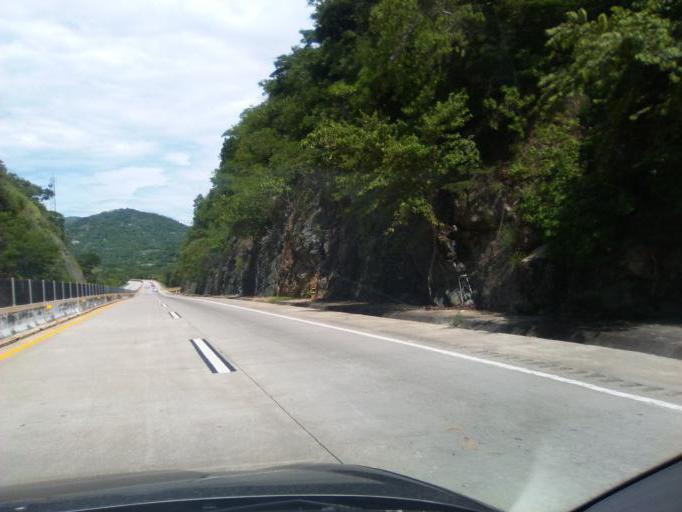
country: MX
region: Guerrero
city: Tierra Colorada
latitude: 17.1353
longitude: -99.5558
